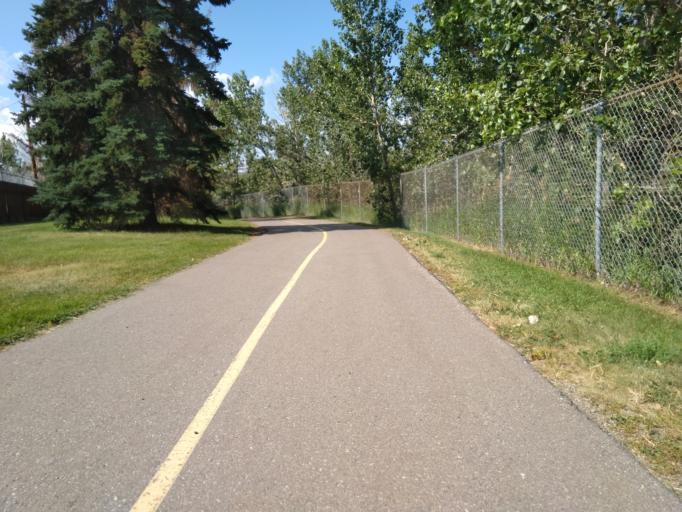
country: CA
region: Alberta
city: Calgary
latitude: 51.0762
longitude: -114.0984
